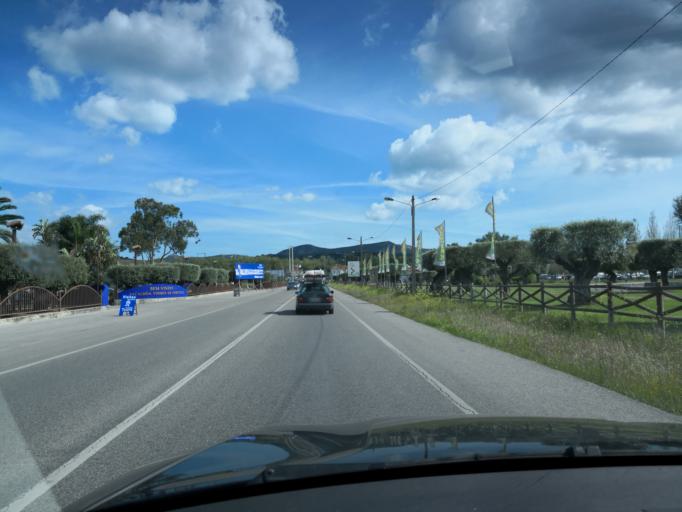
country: PT
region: Setubal
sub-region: Palmela
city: Quinta do Anjo
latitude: 38.5242
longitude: -9.0172
